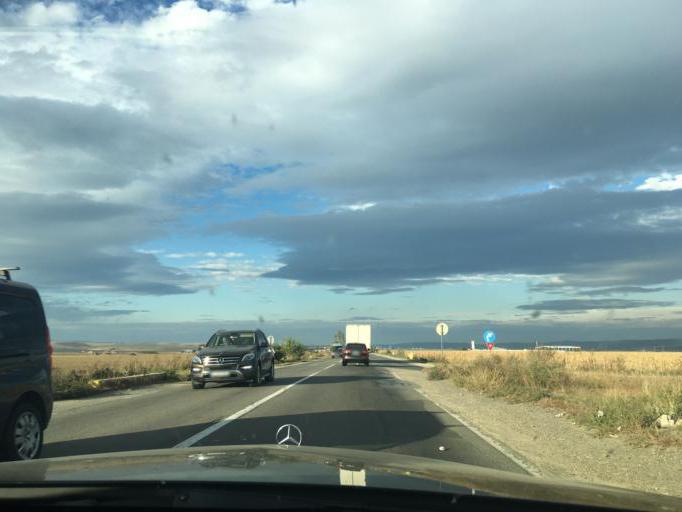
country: RO
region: Alba
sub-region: Comuna Santimbru
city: Santimbru
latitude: 46.1649
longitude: 23.6476
